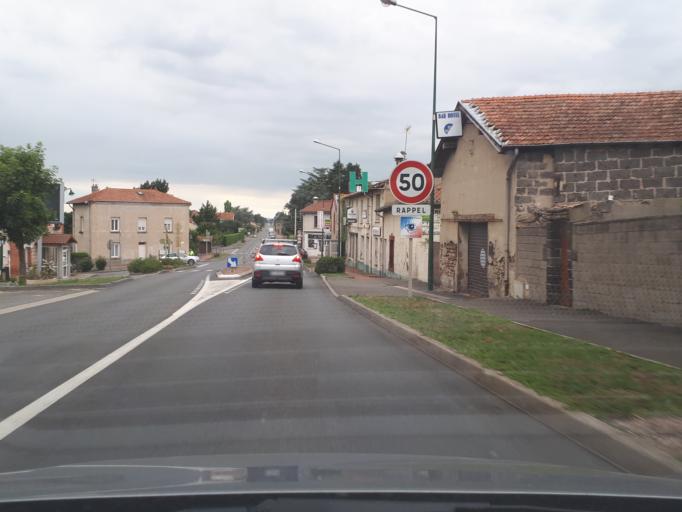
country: FR
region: Rhone-Alpes
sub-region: Departement de la Loire
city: Cuzieu
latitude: 45.6083
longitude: 4.2611
